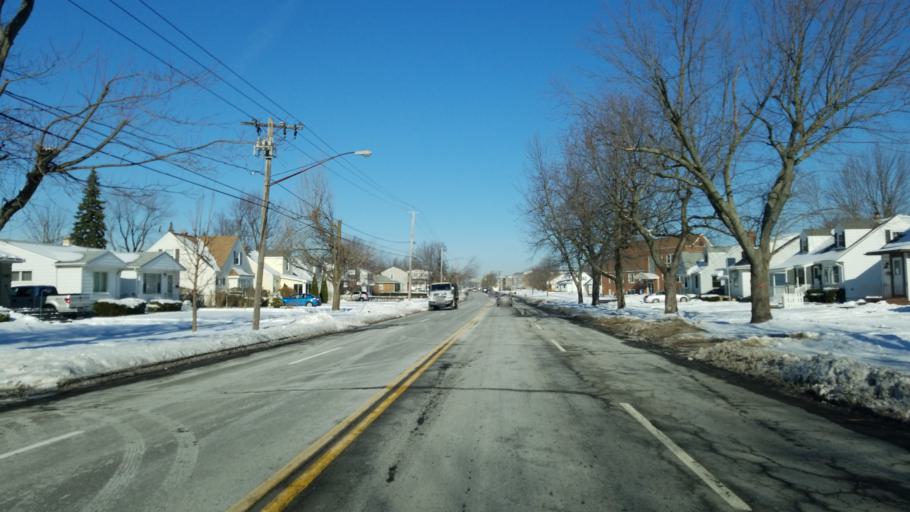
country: US
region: New York
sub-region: Erie County
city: Amherst
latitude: 42.9845
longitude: -78.8306
